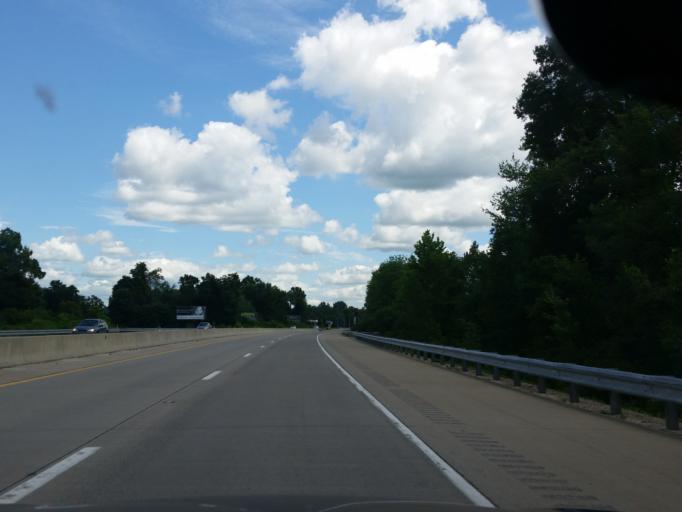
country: US
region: Pennsylvania
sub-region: Dauphin County
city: Millersburg
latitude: 40.6303
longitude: -76.9513
